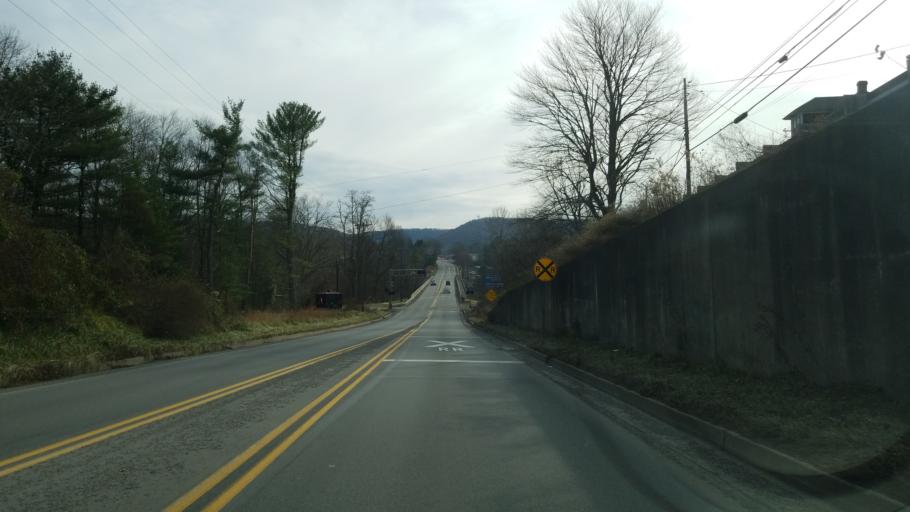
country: US
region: Pennsylvania
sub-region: Clearfield County
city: Clearfield
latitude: 41.0193
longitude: -78.4098
